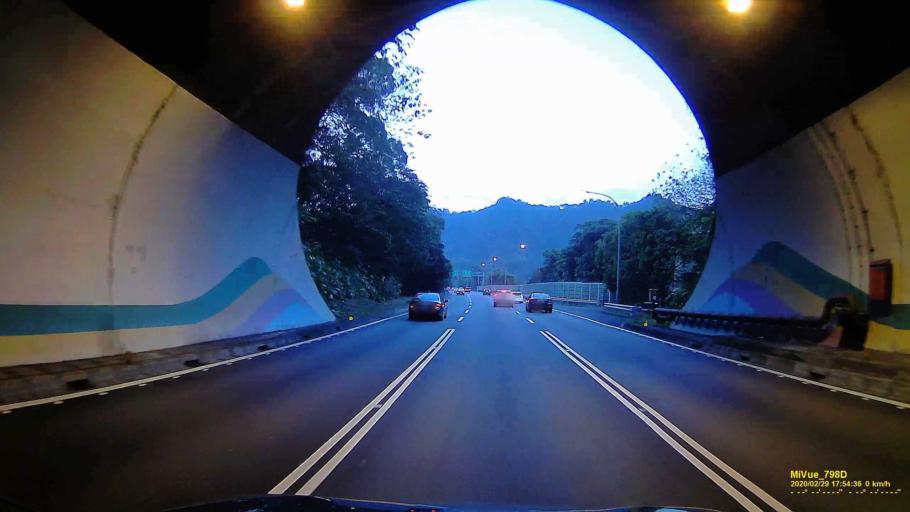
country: TW
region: Taipei
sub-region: Taipei
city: Banqiao
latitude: 24.9823
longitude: 121.4956
